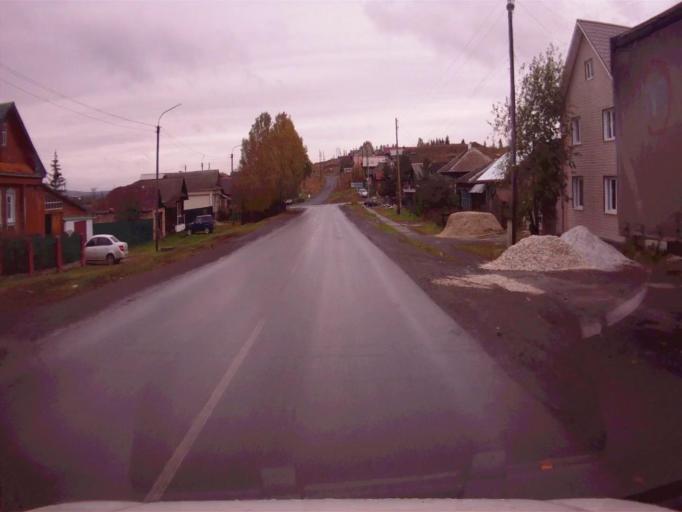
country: RU
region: Chelyabinsk
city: Verkhniy Ufaley
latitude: 56.0574
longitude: 60.2043
